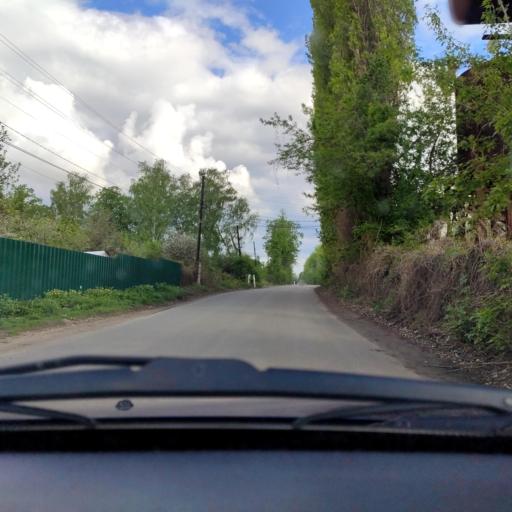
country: RU
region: Voronezj
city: Voronezh
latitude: 51.5990
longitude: 39.1674
